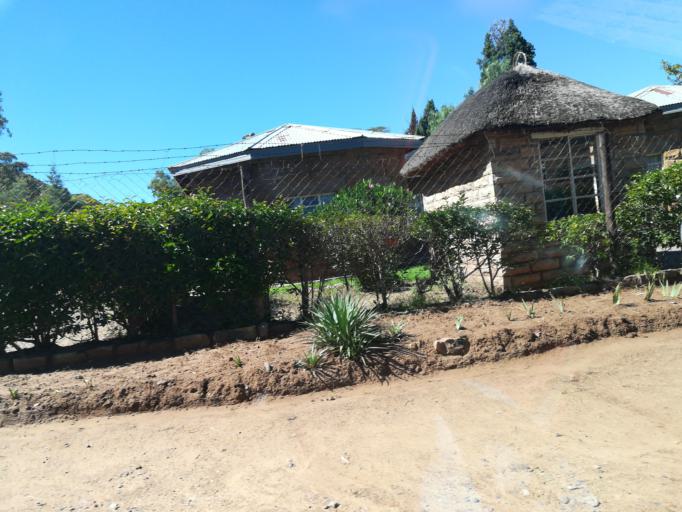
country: LS
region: Quthing
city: Quthing
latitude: -30.3415
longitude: 27.5462
